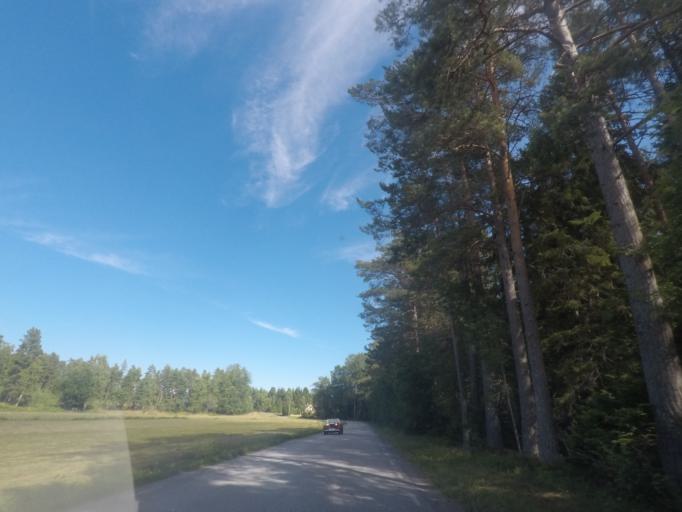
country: SE
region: Stockholm
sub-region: Norrtalje Kommun
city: Arno
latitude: 60.1614
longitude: 18.7510
